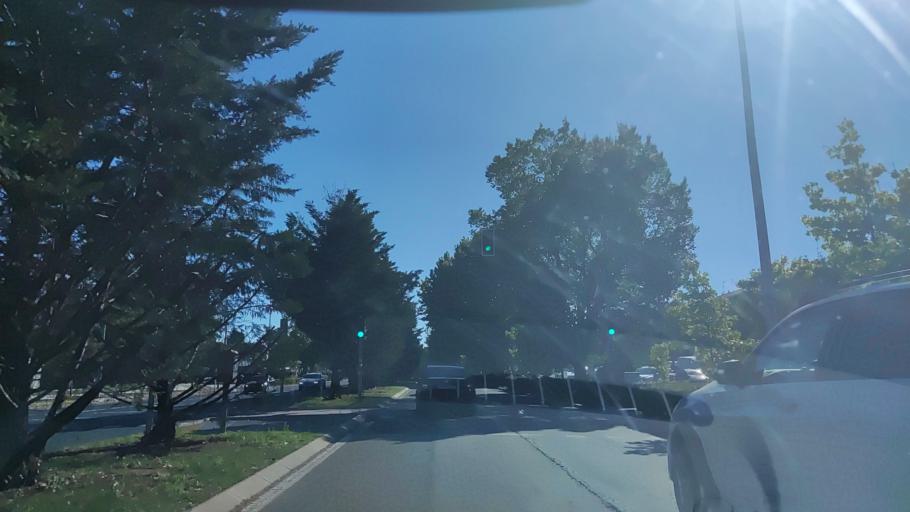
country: ES
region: Madrid
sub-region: Provincia de Madrid
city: Carabanchel
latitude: 40.3845
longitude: -3.7192
